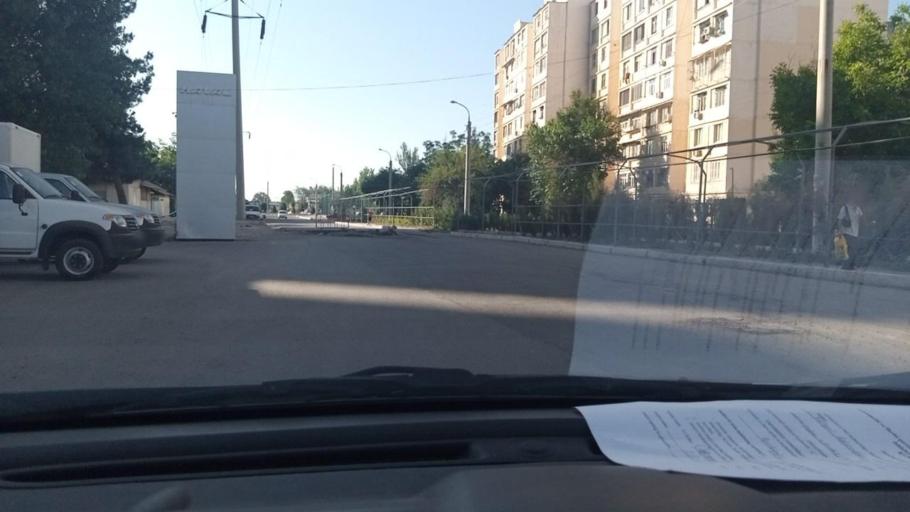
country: UZ
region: Toshkent
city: Salor
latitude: 41.3223
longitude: 69.3597
